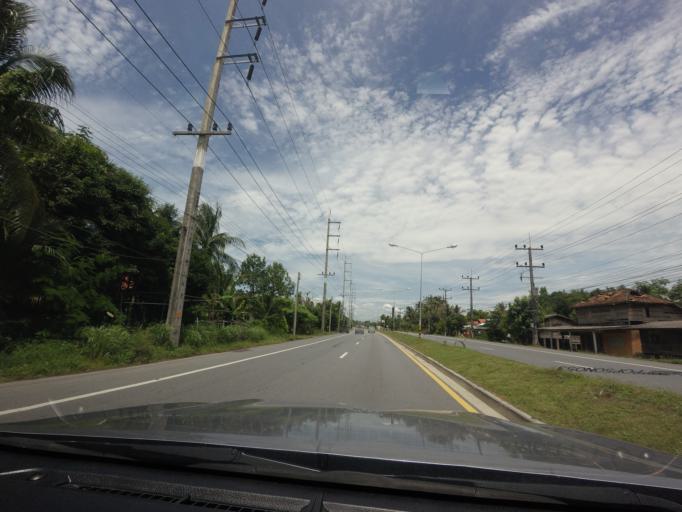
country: TH
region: Songkhla
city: Krasae Sin
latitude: 7.5818
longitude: 100.4070
